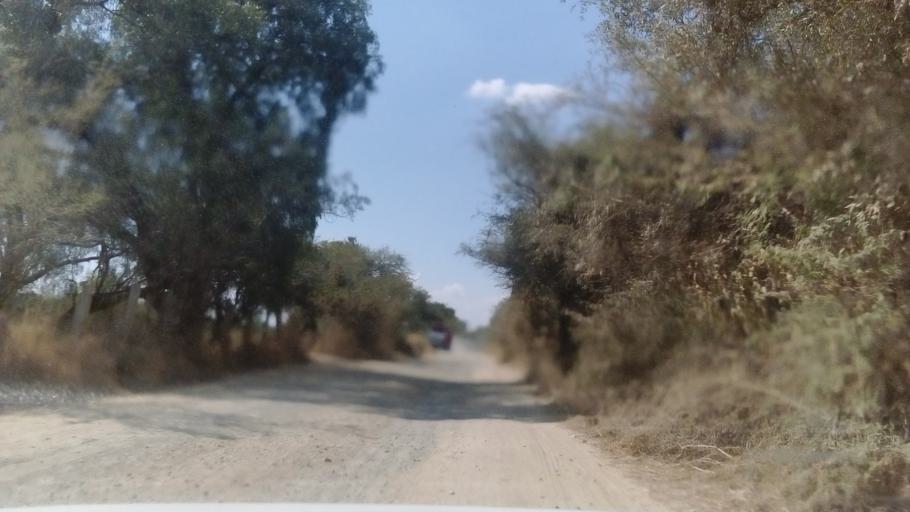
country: MX
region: Guanajuato
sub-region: Silao de la Victoria
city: San Francisco (Banos de Agua Caliente)
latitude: 21.0722
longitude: -101.4657
